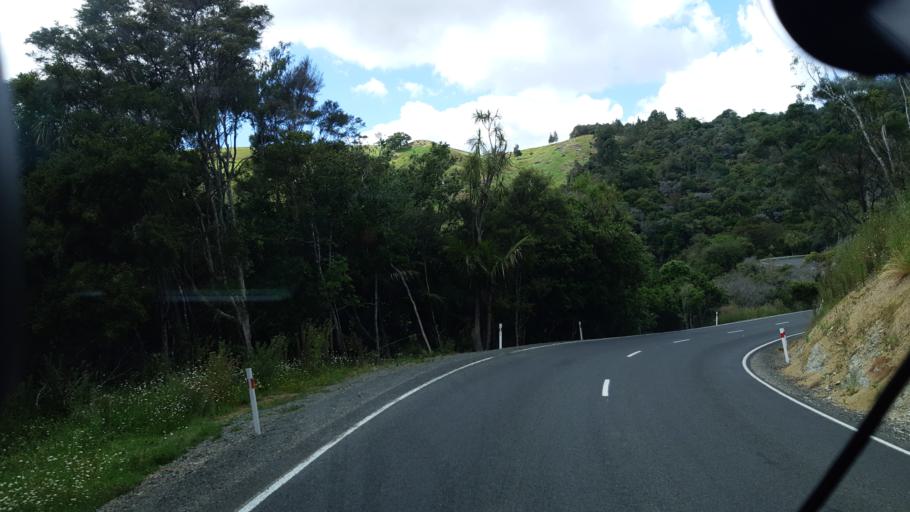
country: NZ
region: Northland
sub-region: Far North District
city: Taipa
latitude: -35.2443
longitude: 173.5353
